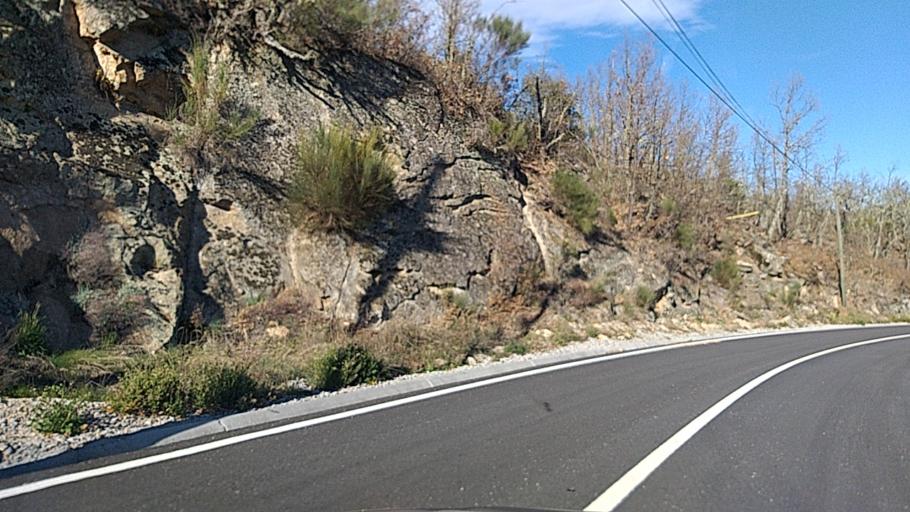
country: ES
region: Castille and Leon
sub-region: Provincia de Salamanca
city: Fuentes de Onoro
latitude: 40.6082
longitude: -6.9246
